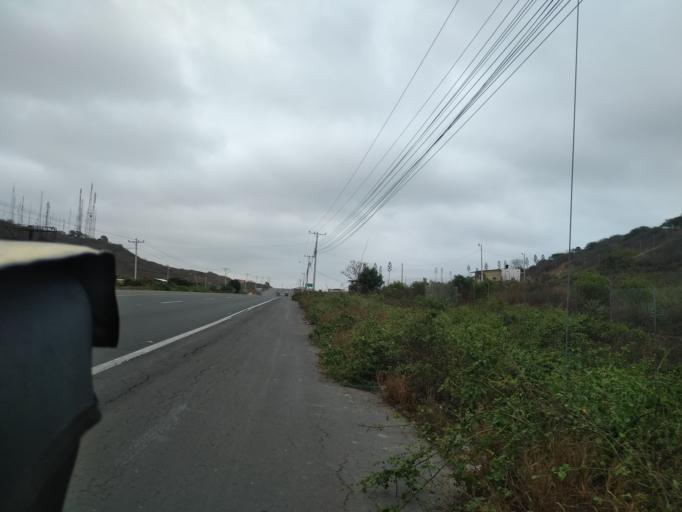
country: EC
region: Santa Elena
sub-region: Canton Santa Elena
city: Santa Elena
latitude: -2.2057
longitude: -80.8574
